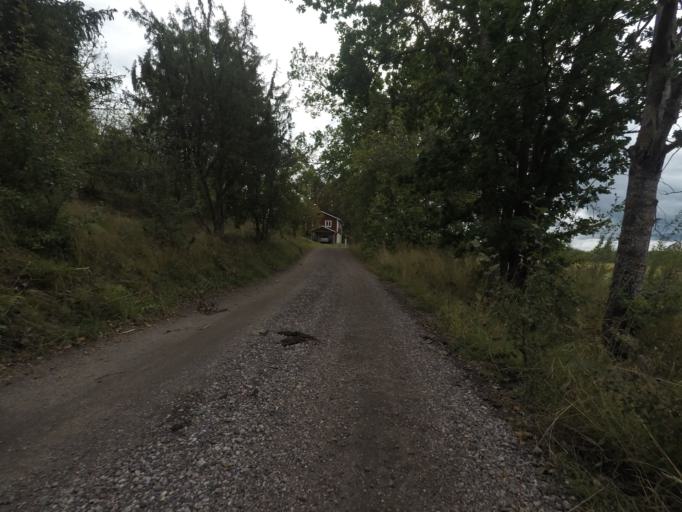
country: SE
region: Vaestmanland
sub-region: Kungsors Kommun
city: Kungsoer
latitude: 59.4625
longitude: 16.0707
